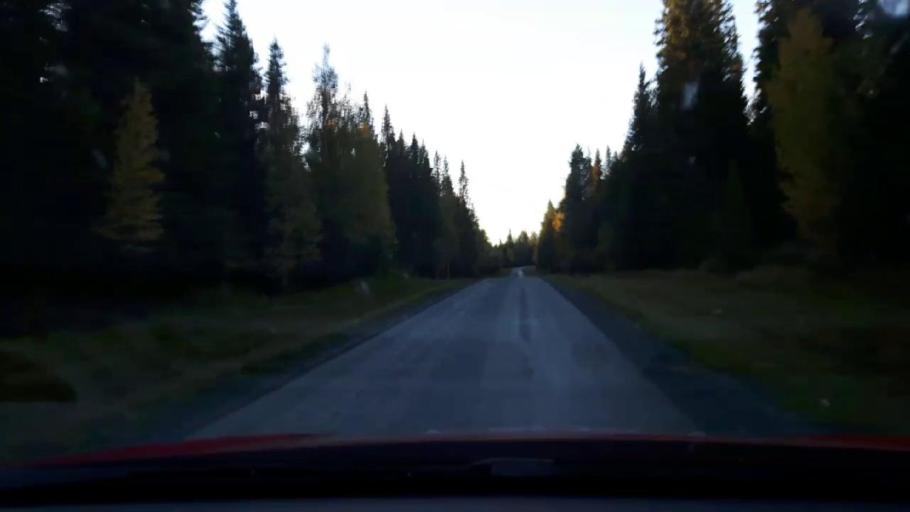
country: SE
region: Jaemtland
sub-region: Krokoms Kommun
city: Krokom
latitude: 63.4669
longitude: 14.3562
